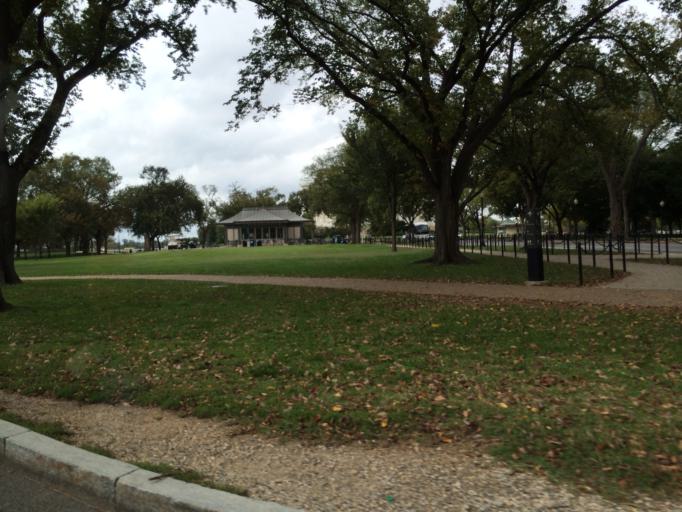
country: US
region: Washington, D.C.
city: Washington, D.C.
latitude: 38.8872
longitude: -77.0484
